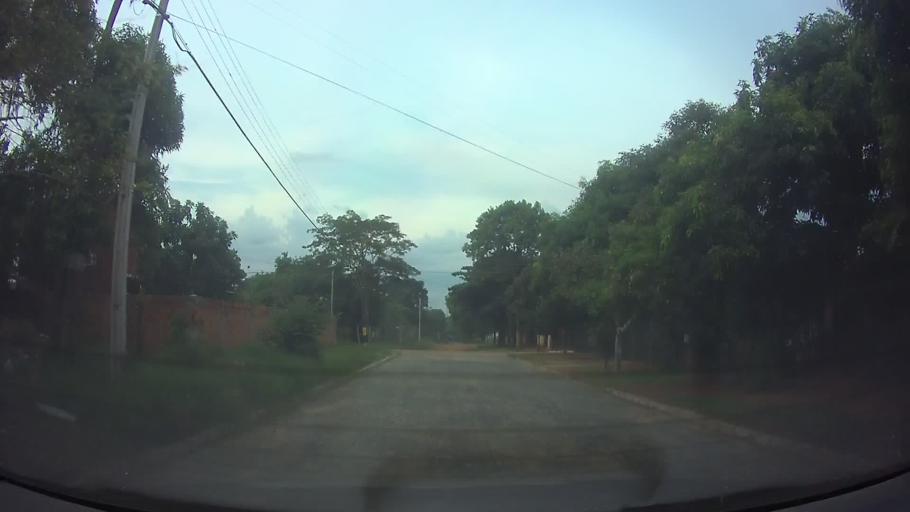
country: PY
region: Central
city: San Lorenzo
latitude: -25.2629
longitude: -57.4619
